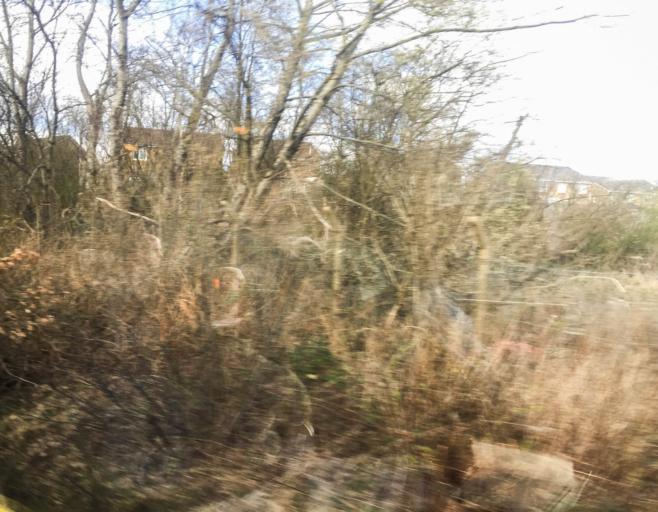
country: GB
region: Scotland
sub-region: West Dunbartonshire
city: Old Kilpatrick
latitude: 55.9199
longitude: -4.4452
